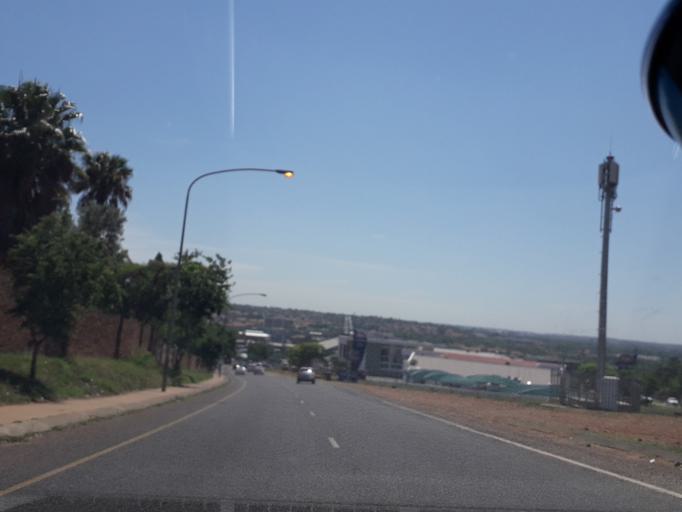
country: ZA
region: Gauteng
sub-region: City of Tshwane Metropolitan Municipality
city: Centurion
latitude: -25.8656
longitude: 28.1832
